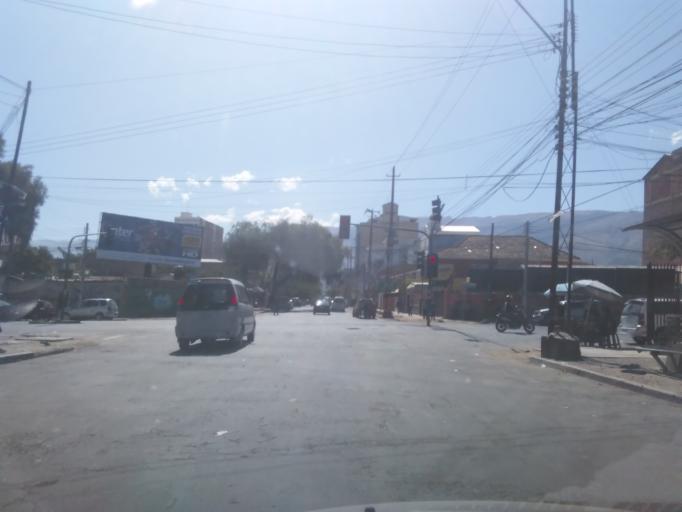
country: BO
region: Cochabamba
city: Cochabamba
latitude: -17.3987
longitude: -66.1484
